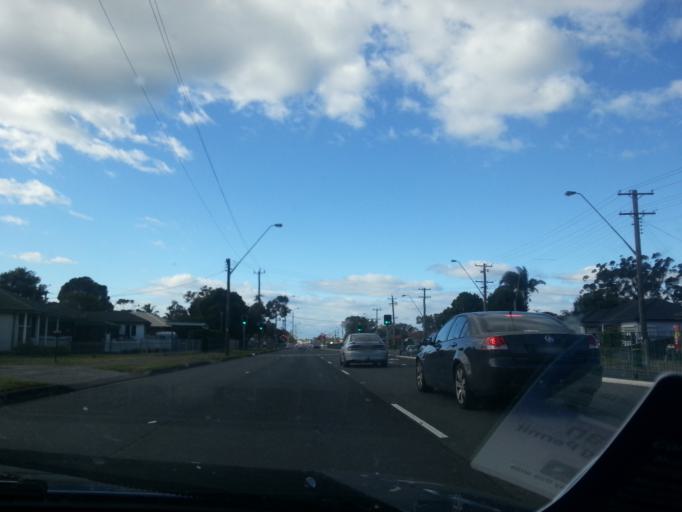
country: AU
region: New South Wales
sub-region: Shellharbour
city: Lake Illawarra
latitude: -34.5545
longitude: 150.8525
